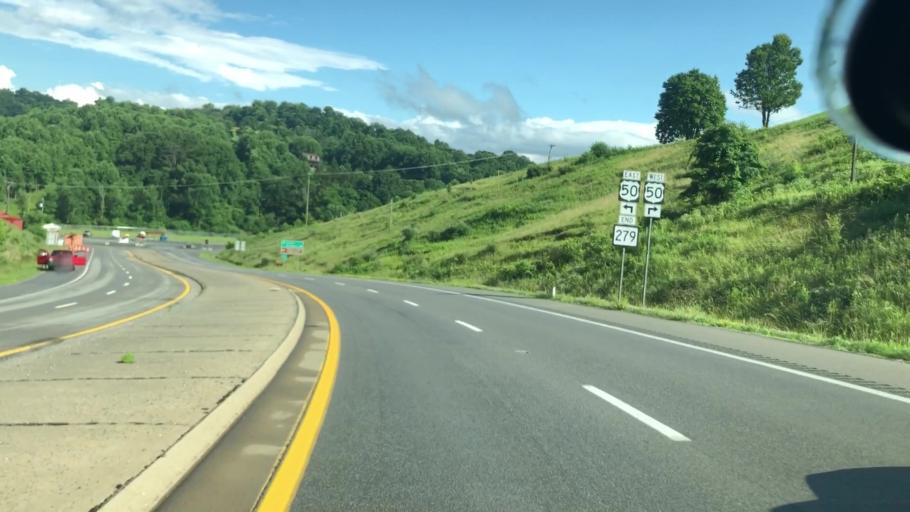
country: US
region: West Virginia
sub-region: Harrison County
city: Bridgeport
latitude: 39.2992
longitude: -80.2064
